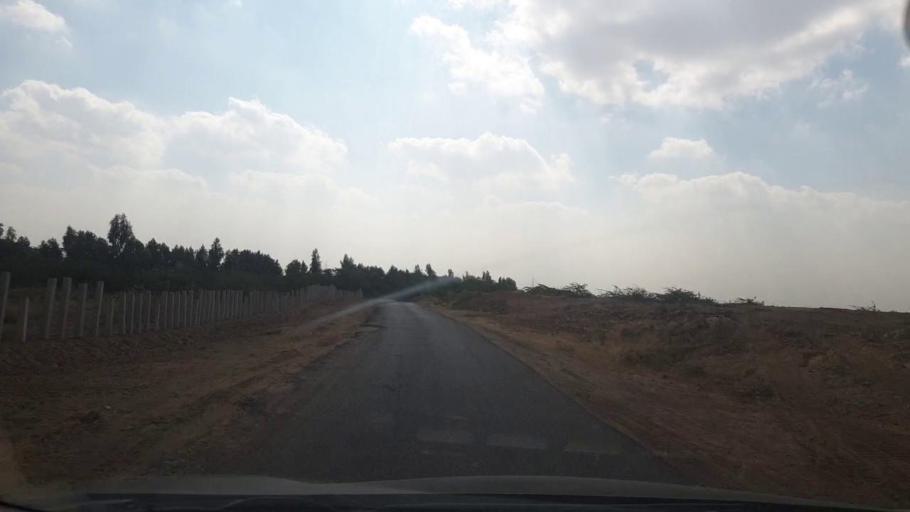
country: PK
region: Sindh
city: Malir Cantonment
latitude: 25.0224
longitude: 67.3546
